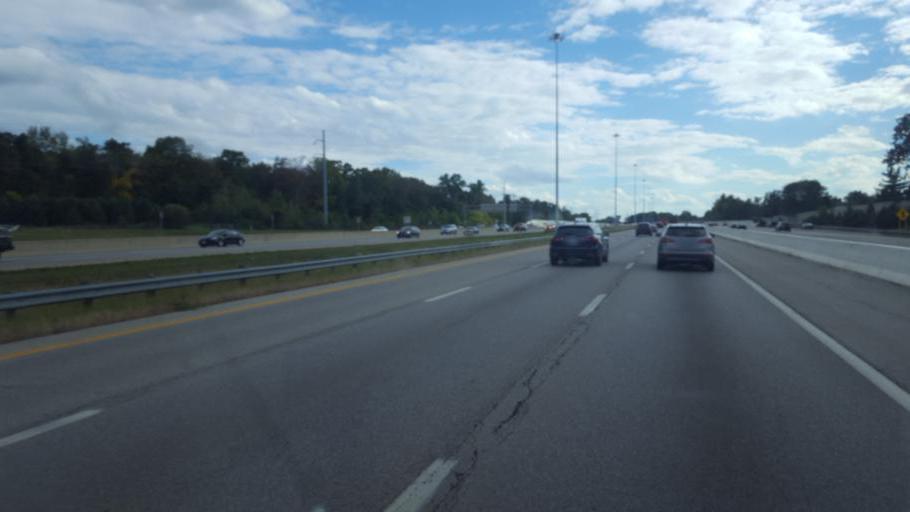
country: US
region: Ohio
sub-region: Franklin County
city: Huber Ridge
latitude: 40.0797
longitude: -82.9075
